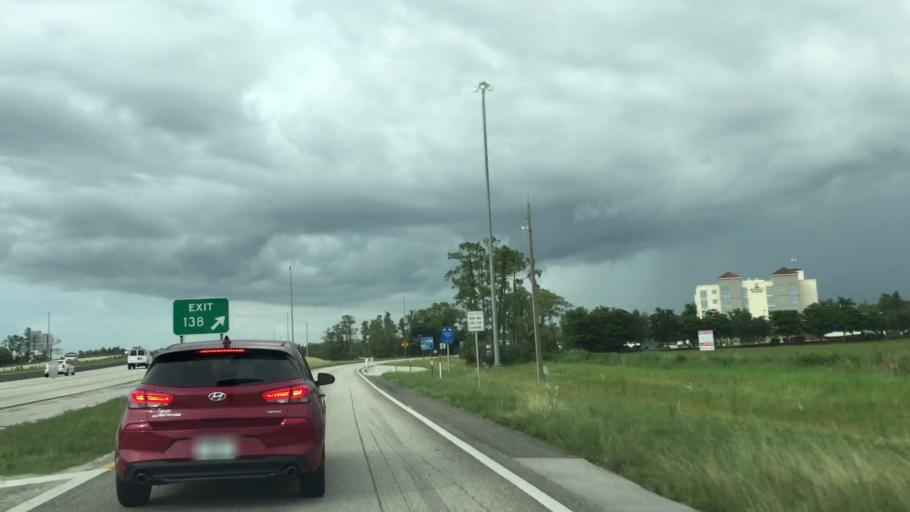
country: US
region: Florida
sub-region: Lee County
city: Fort Myers
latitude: 26.6310
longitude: -81.8036
